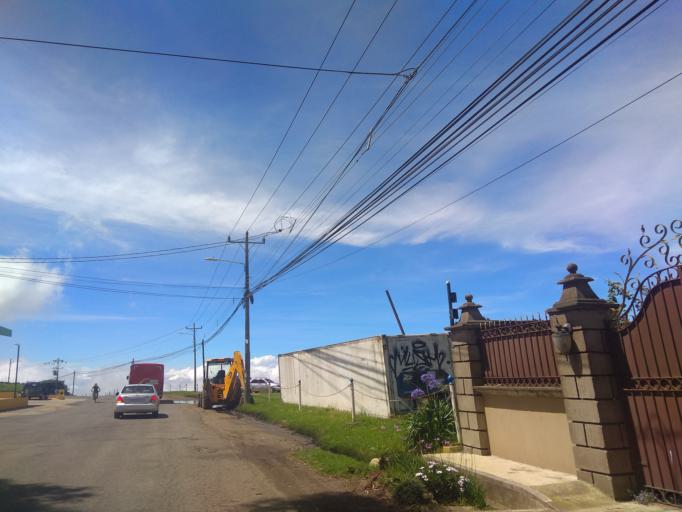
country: CR
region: Cartago
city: Cot
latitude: 9.9125
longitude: -83.8873
